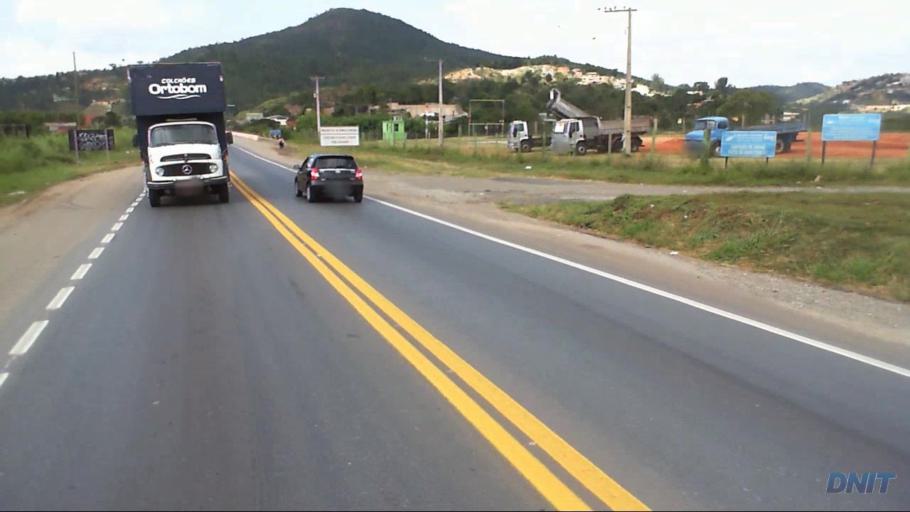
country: BR
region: Minas Gerais
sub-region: Santa Luzia
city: Santa Luzia
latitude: -19.8413
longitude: -43.8703
